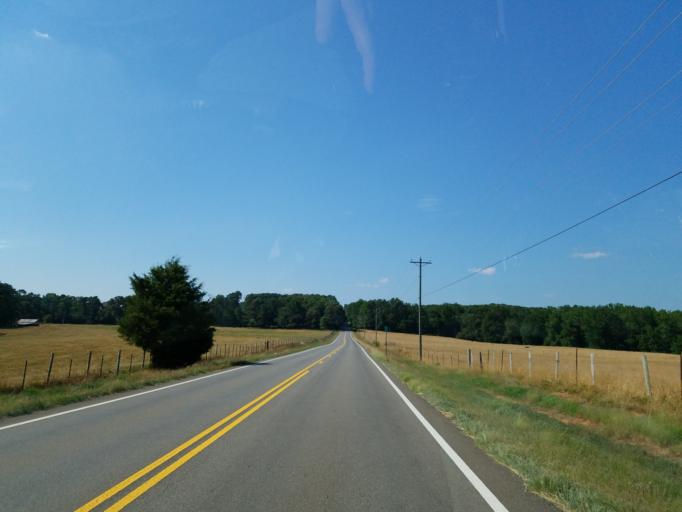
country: US
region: Georgia
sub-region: Fulton County
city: Milton
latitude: 34.2161
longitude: -84.2896
